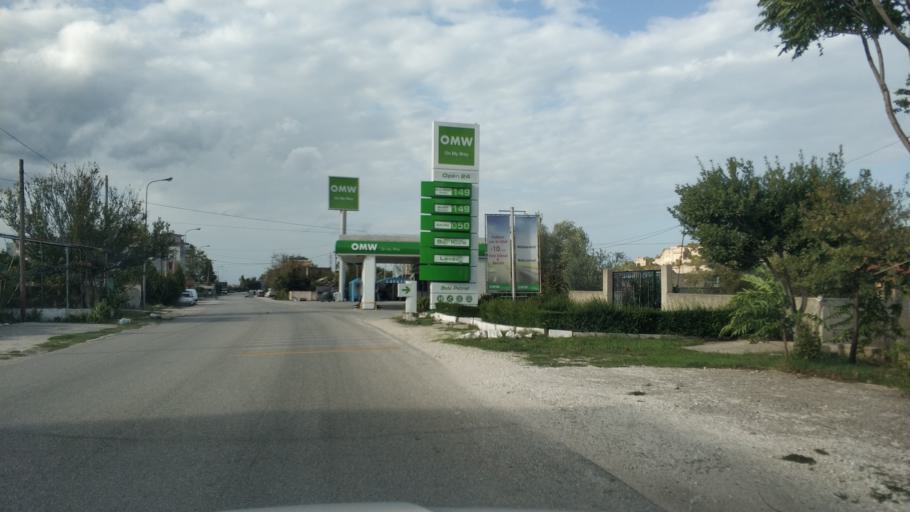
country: AL
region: Vlore
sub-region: Rrethi i Vlores
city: Orikum
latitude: 40.3289
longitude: 19.4782
